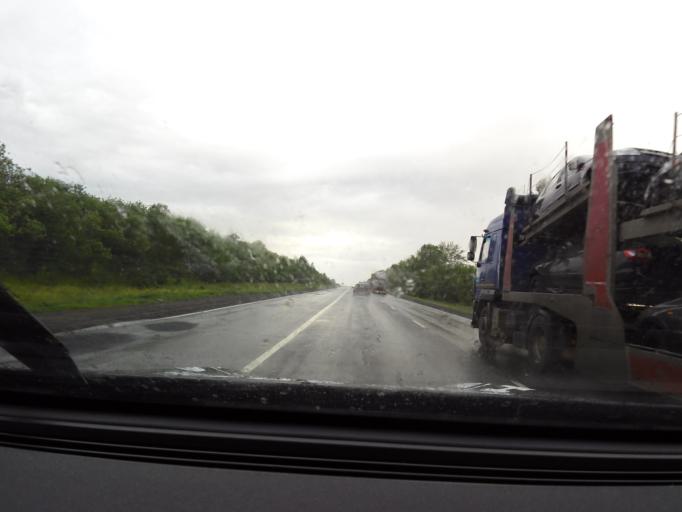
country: RU
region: Chuvashia
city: Yantikovo
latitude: 55.8013
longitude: 47.8790
